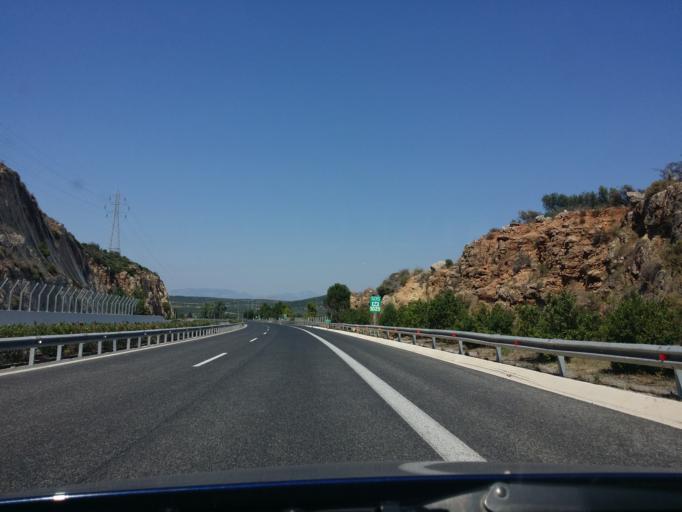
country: GR
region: Peloponnese
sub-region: Nomos Korinthias
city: Nemea
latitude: 37.7852
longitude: 22.7076
